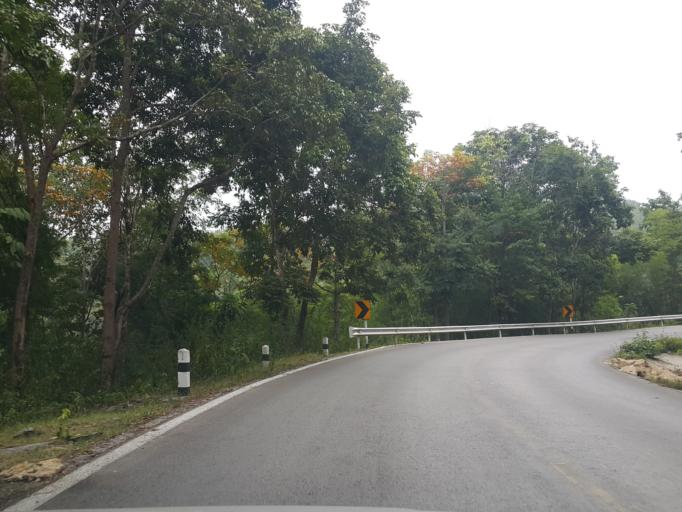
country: TH
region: Mae Hong Son
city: Mae Hi
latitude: 19.2699
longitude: 98.5024
